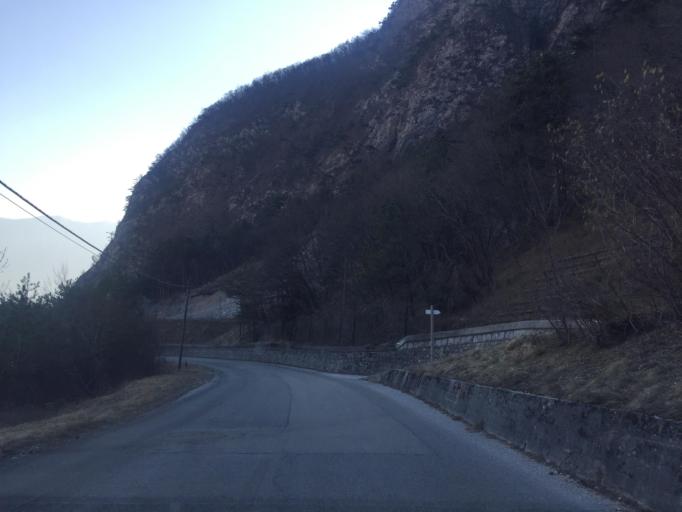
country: IT
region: Friuli Venezia Giulia
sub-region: Provincia di Udine
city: Tolmezzo
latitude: 46.4105
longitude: 13.0424
